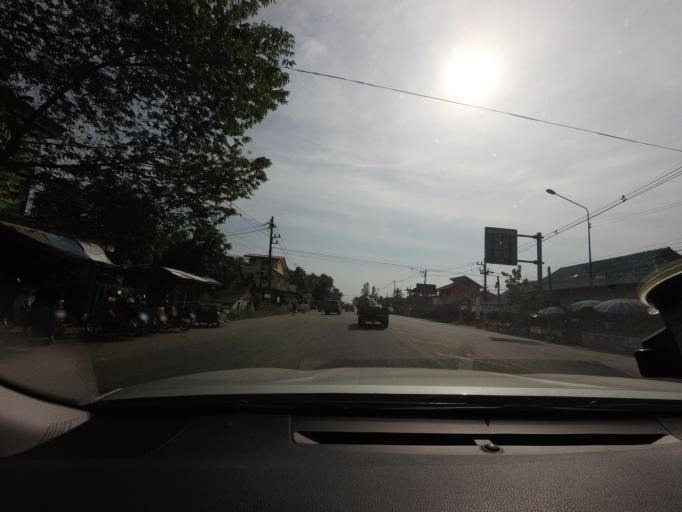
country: TH
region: Narathiwat
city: Narathiwat
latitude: 6.3801
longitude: 101.8030
